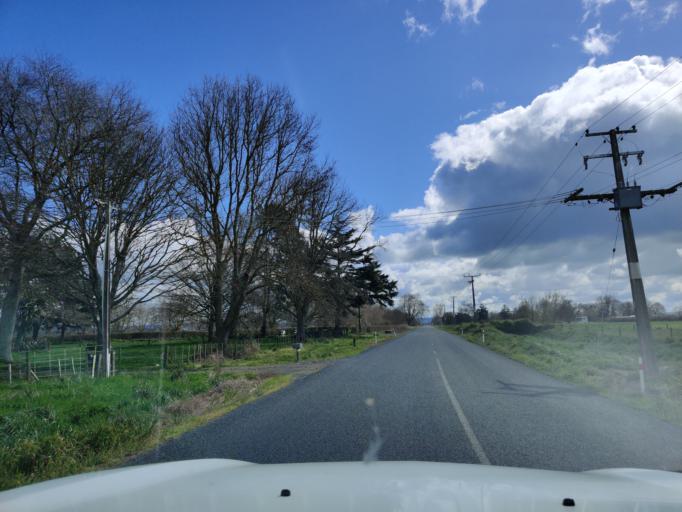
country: NZ
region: Waikato
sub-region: Waikato District
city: Ngaruawahia
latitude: -37.6160
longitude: 175.3149
